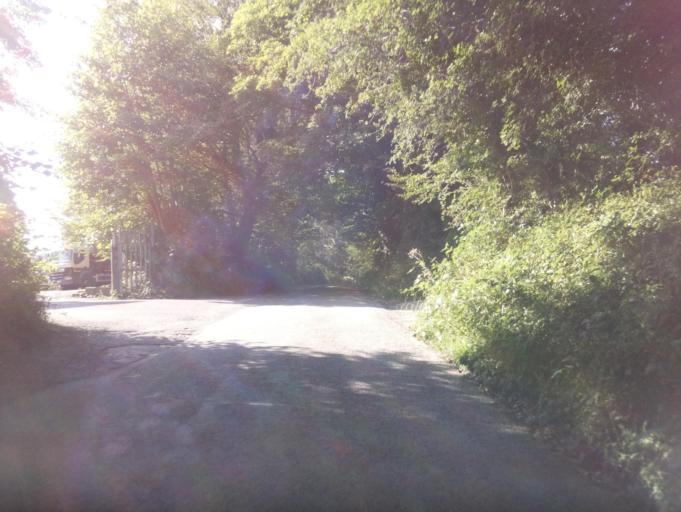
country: GB
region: England
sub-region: Devon
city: Buckfastleigh
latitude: 50.4402
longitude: -3.7866
